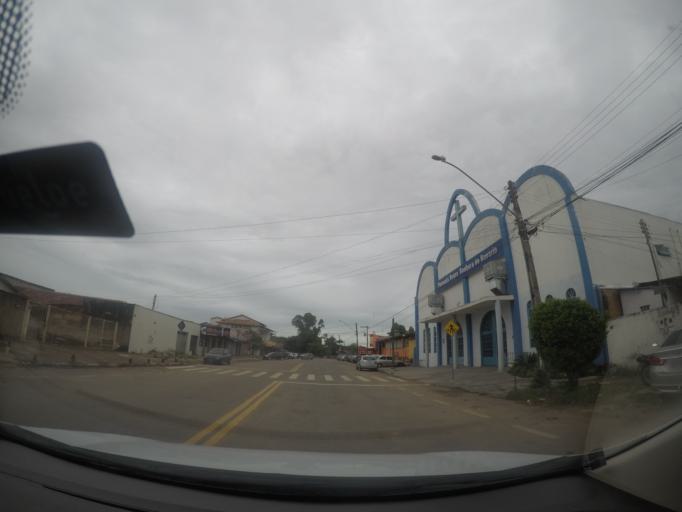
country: BR
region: Goias
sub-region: Goiania
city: Goiania
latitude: -16.6831
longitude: -49.3289
